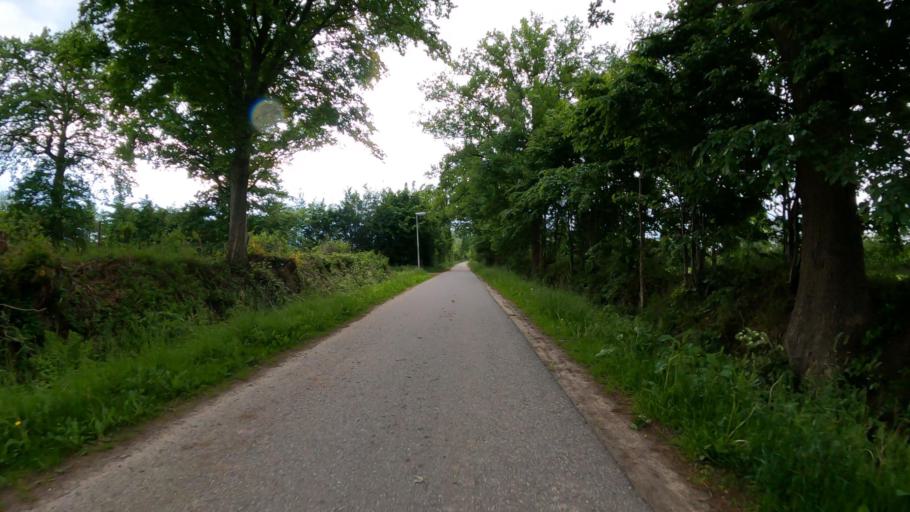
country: DE
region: Schleswig-Holstein
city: Appen
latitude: 53.6554
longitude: 9.7604
